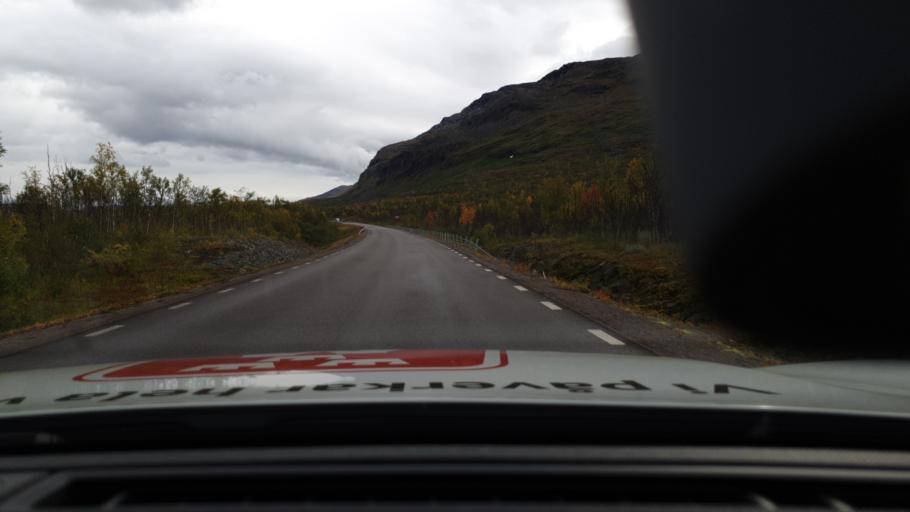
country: NO
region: Troms
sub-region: Bardu
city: Setermoen
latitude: 68.4267
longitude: 18.3389
